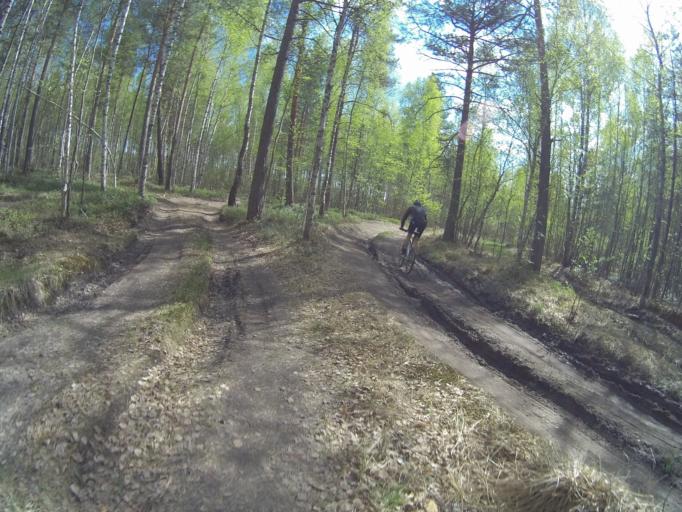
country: RU
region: Vladimir
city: Vorsha
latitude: 55.9493
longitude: 40.1938
